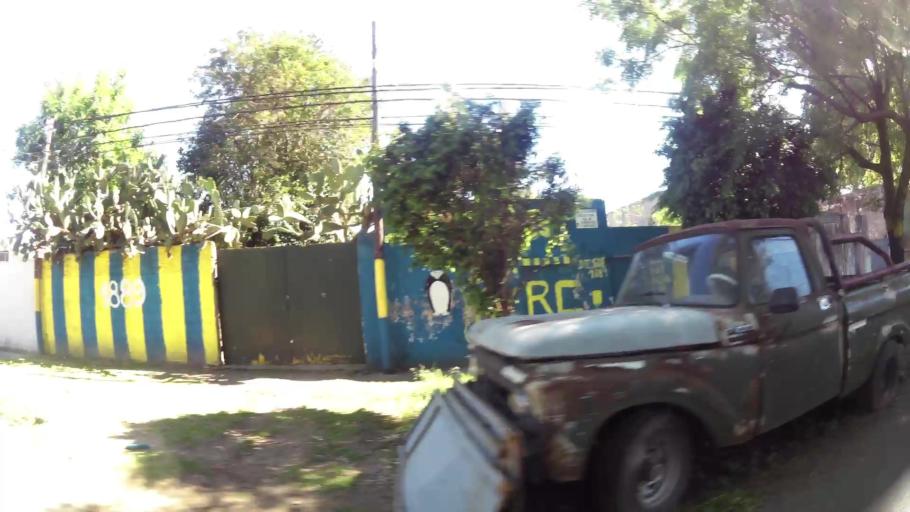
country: AR
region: Santa Fe
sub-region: Departamento de Rosario
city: Rosario
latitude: -32.9521
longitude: -60.6902
